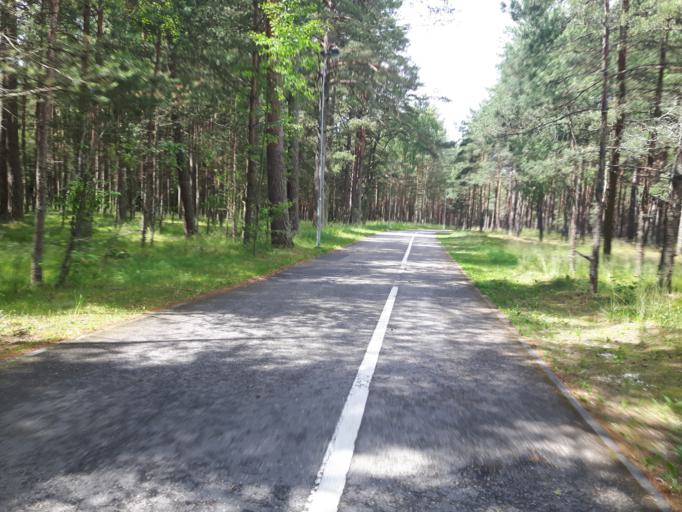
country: LT
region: Klaipedos apskritis
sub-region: Klaipeda
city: Klaipeda
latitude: 55.7593
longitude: 21.1079
